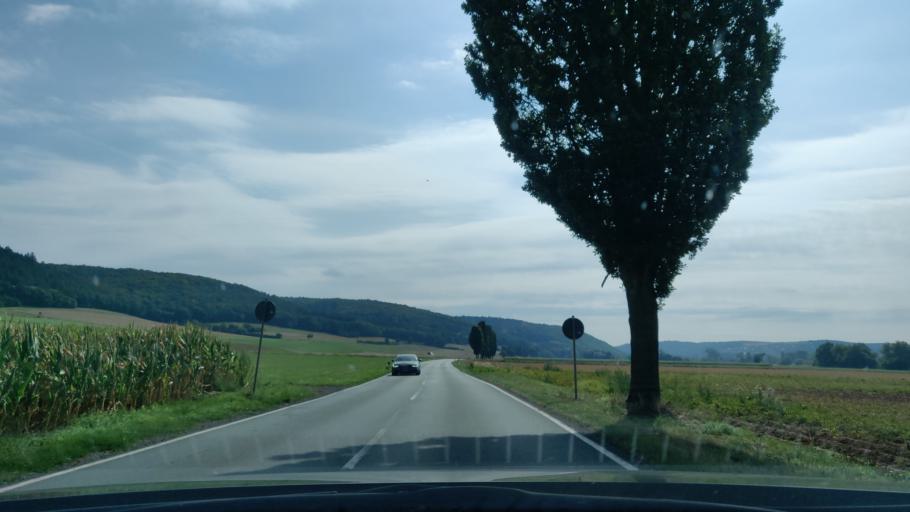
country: DE
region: Hesse
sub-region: Regierungsbezirk Kassel
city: Bad Wildungen
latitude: 51.1419
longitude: 9.1817
